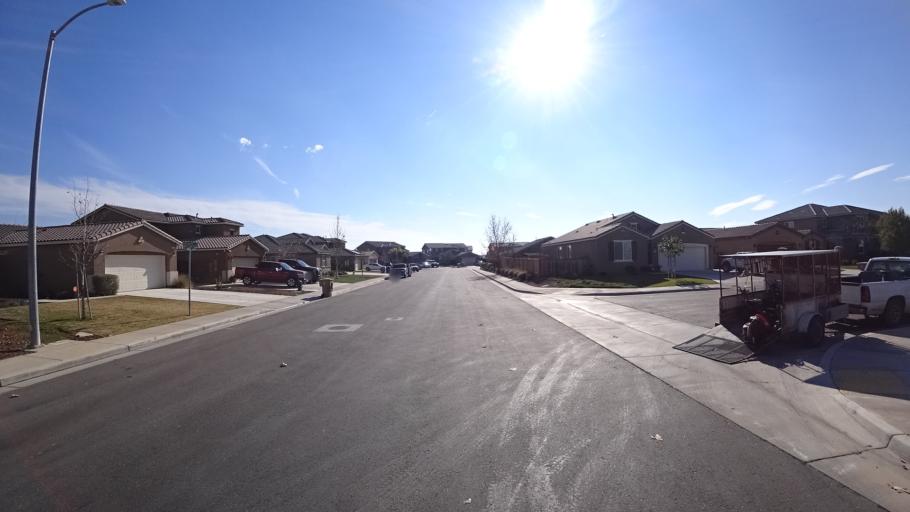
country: US
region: California
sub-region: Kern County
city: Oildale
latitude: 35.4107
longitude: -118.8971
